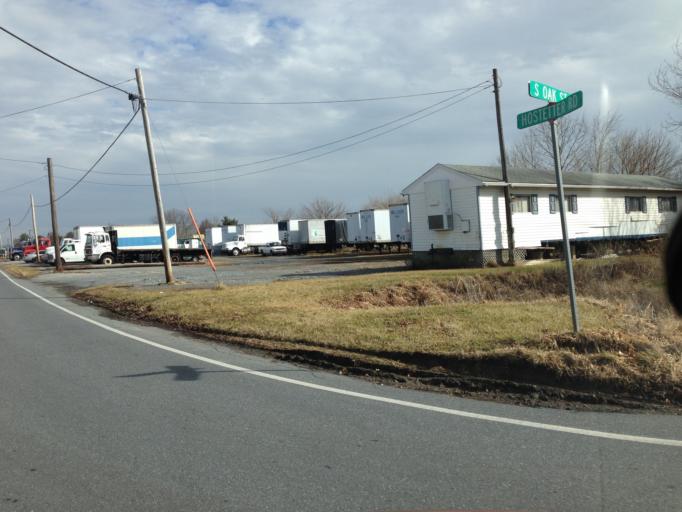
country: US
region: Pennsylvania
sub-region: Lancaster County
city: Manheim
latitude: 40.1611
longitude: -76.3858
